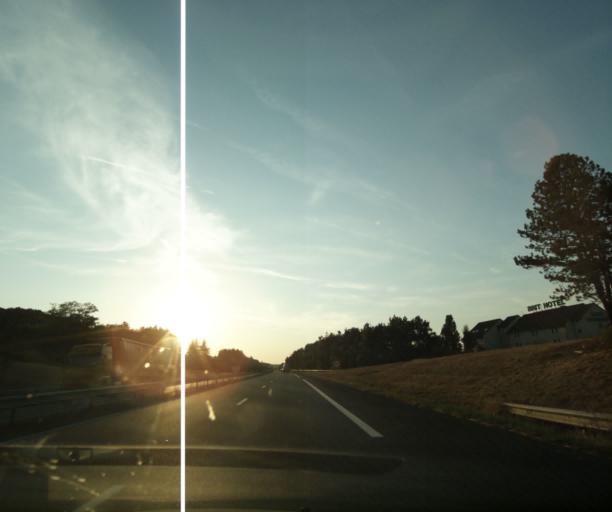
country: FR
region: Aquitaine
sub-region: Departement du Lot-et-Garonne
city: Boe
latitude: 44.1625
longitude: 0.6037
